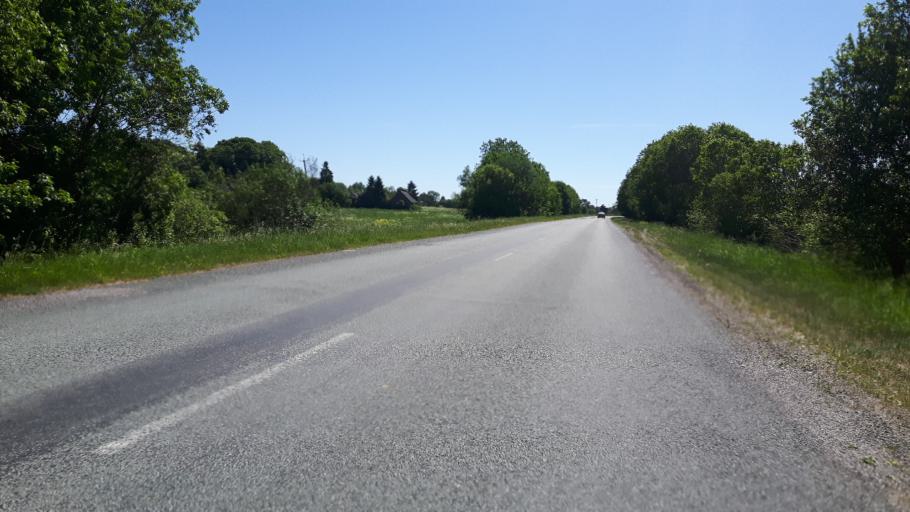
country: EE
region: Harju
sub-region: Kuusalu vald
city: Kuusalu
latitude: 59.5099
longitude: 25.5198
